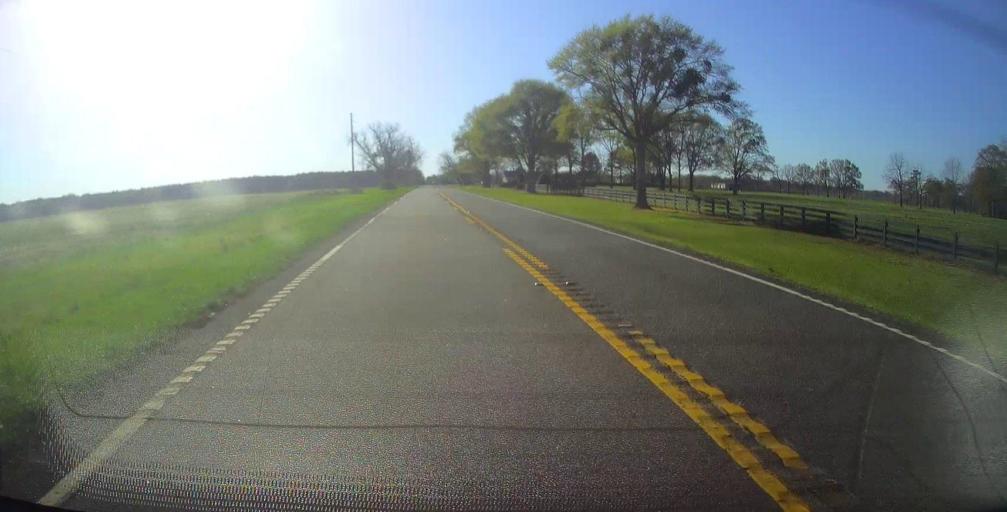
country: US
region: Georgia
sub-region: Houston County
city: Perry
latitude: 32.4391
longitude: -83.8281
